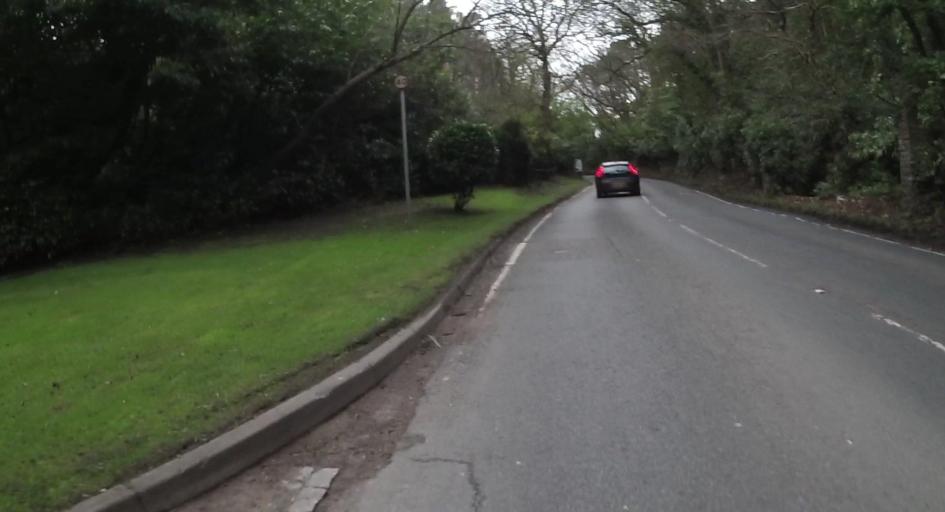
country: GB
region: England
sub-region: Surrey
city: Farnham
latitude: 51.1836
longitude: -0.7914
